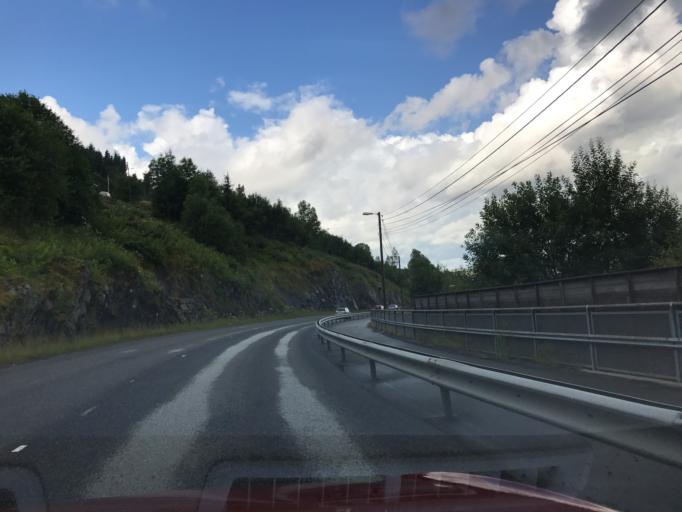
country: NO
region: Hordaland
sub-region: Bergen
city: Sandsli
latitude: 60.3005
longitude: 5.3751
